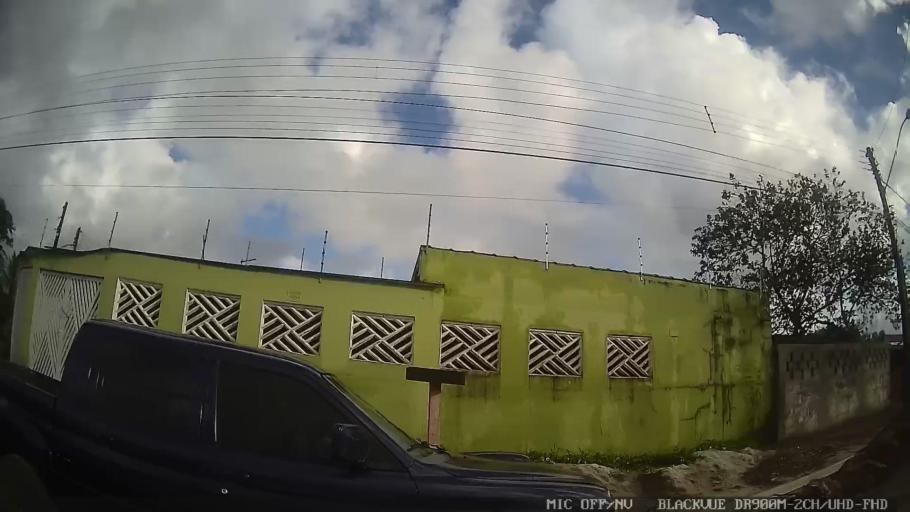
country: BR
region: Sao Paulo
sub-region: Itanhaem
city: Itanhaem
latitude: -24.1710
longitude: -46.8470
